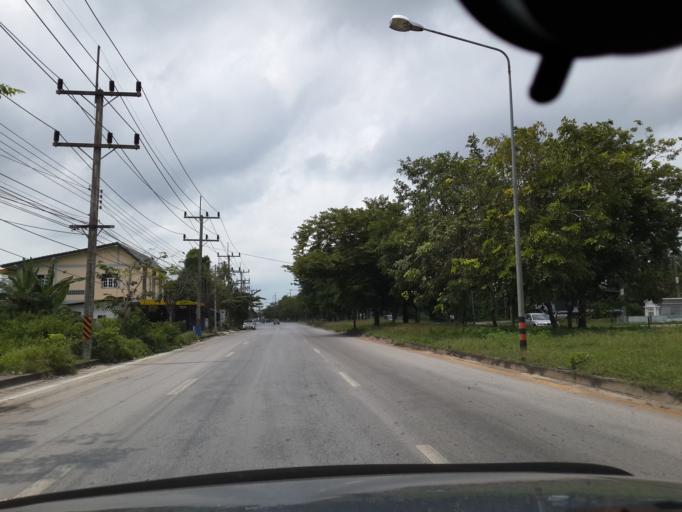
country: TH
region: Pattani
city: Pattani
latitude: 6.8700
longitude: 101.2801
